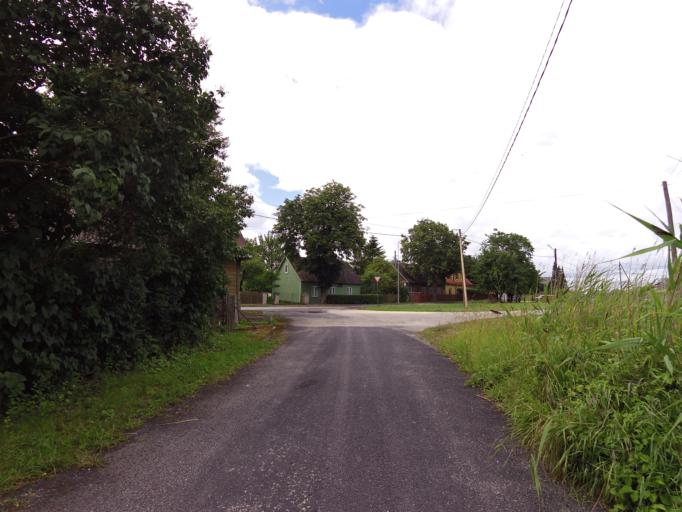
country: EE
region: Laeaene
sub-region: Haapsalu linn
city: Haapsalu
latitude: 58.9560
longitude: 23.5261
